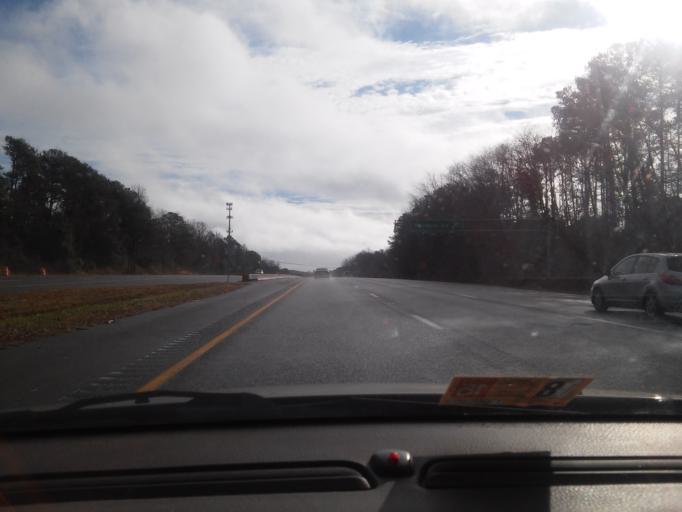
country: US
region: Virginia
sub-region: Henrico County
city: Tuckahoe
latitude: 37.6267
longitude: -77.5593
